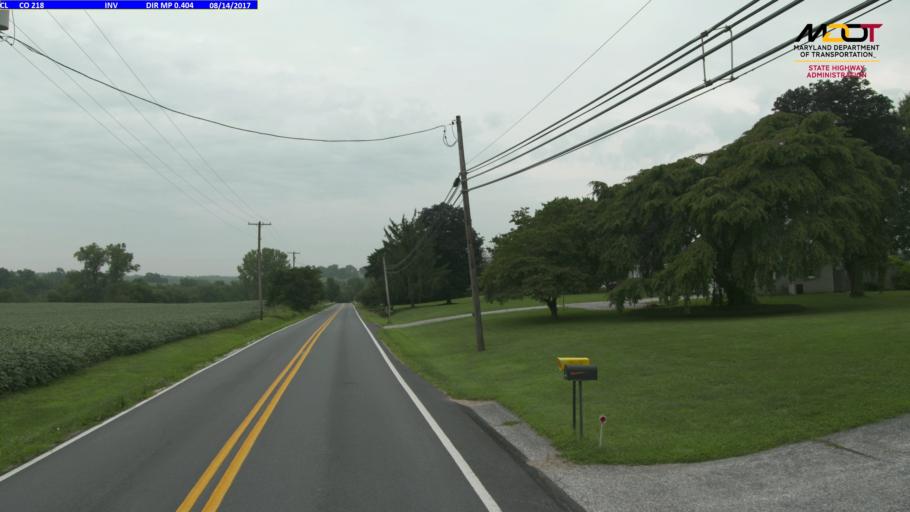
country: US
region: Maryland
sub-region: Carroll County
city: Taneytown
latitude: 39.5889
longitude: -77.1825
